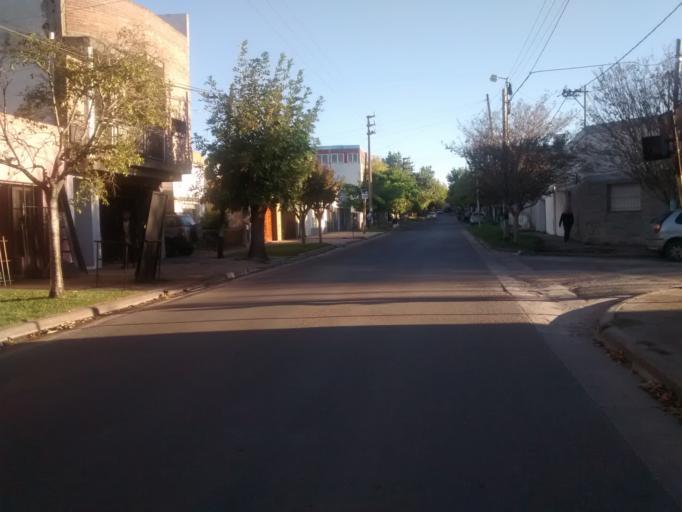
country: AR
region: Buenos Aires
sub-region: Partido de La Plata
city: La Plata
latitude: -34.9085
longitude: -57.9205
